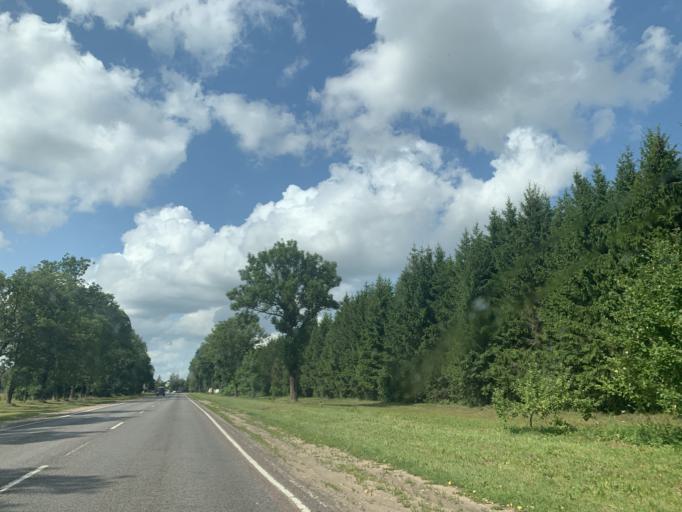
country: BY
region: Minsk
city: Enyerhyetykaw
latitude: 53.5810
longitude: 27.0555
